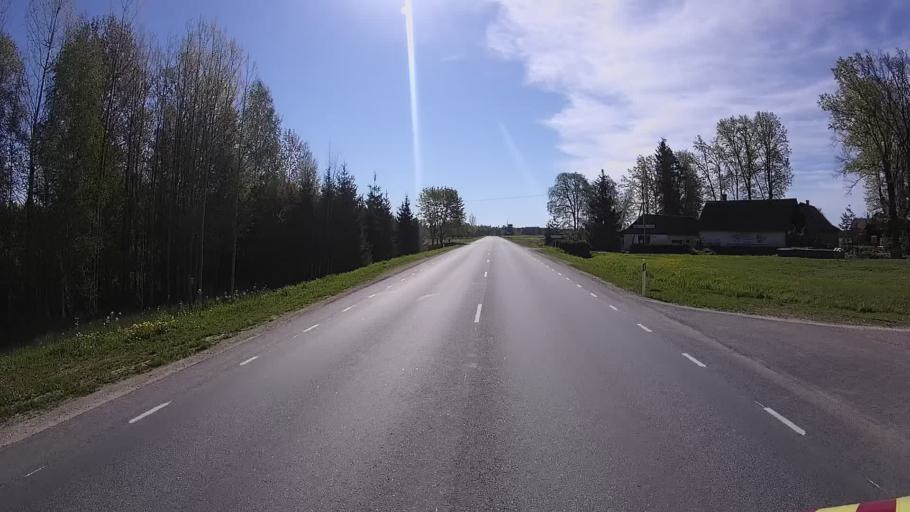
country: EE
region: Tartu
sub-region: UElenurme vald
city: Ulenurme
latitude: 58.3404
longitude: 26.9585
